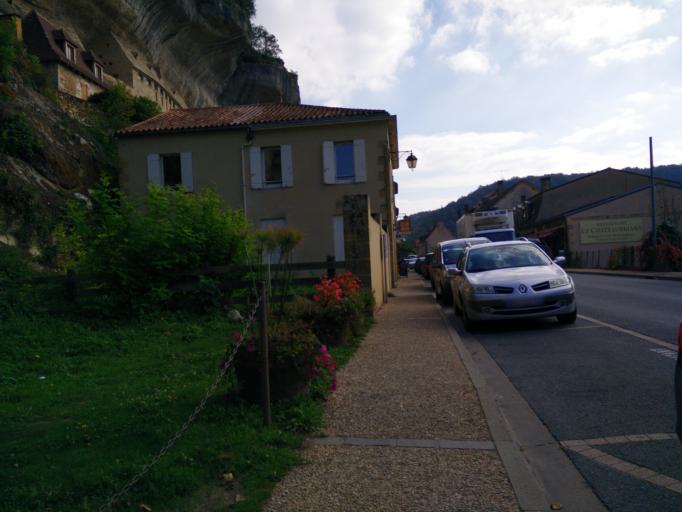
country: FR
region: Aquitaine
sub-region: Departement de la Dordogne
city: Saint-Cyprien
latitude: 44.9373
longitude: 1.0122
